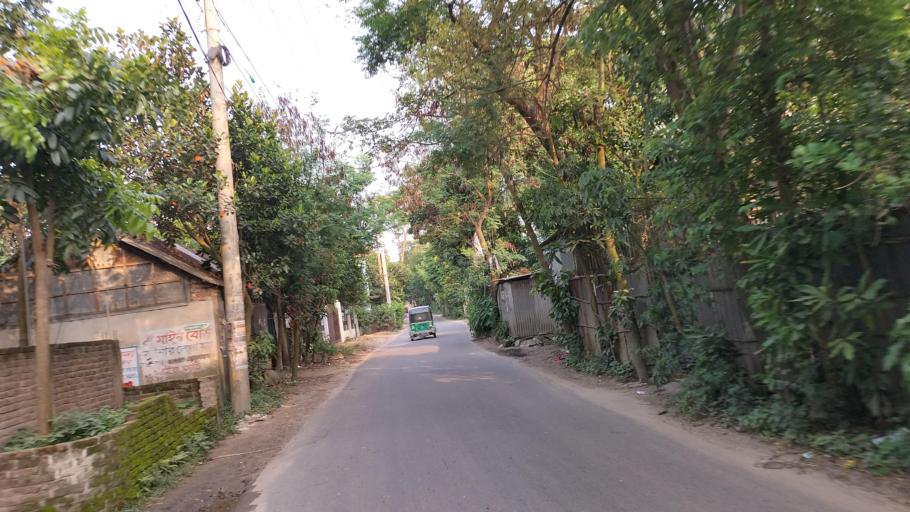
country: BD
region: Dhaka
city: Azimpur
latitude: 23.6656
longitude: 90.3290
